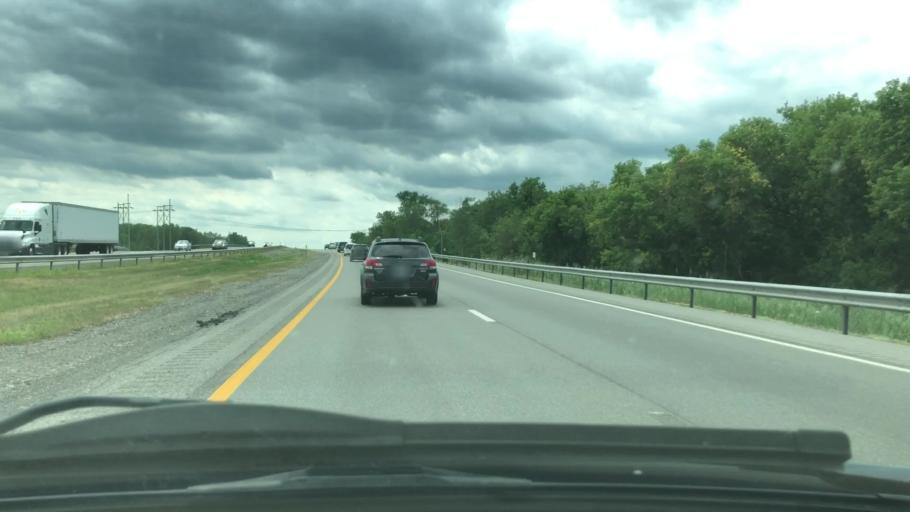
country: US
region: New York
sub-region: Erie County
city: Akron
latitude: 43.0065
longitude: -78.4074
